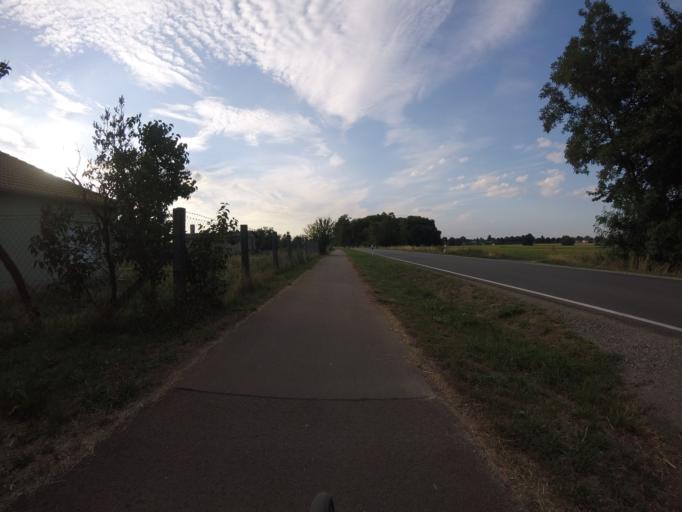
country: DE
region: Brandenburg
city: Altlandsberg
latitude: 52.5732
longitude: 13.7157
